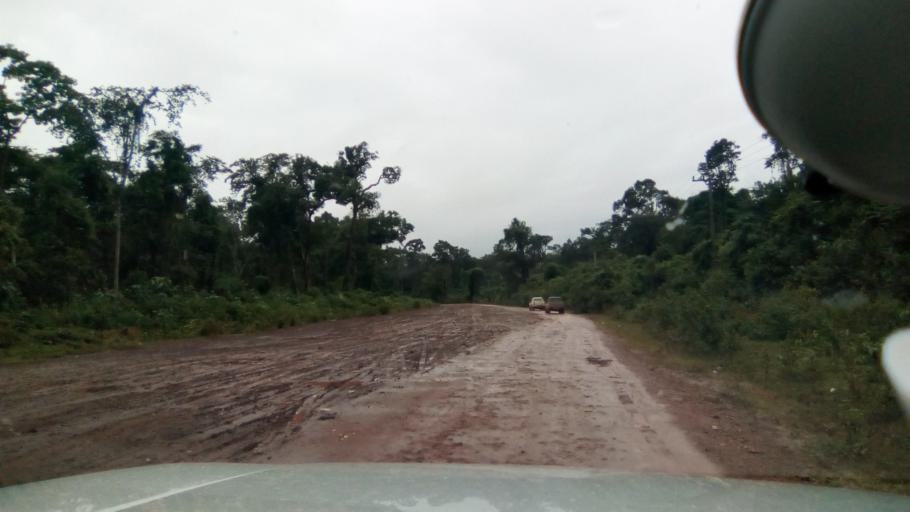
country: LA
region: Attapu
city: Attapu
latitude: 14.6815
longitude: 106.5567
